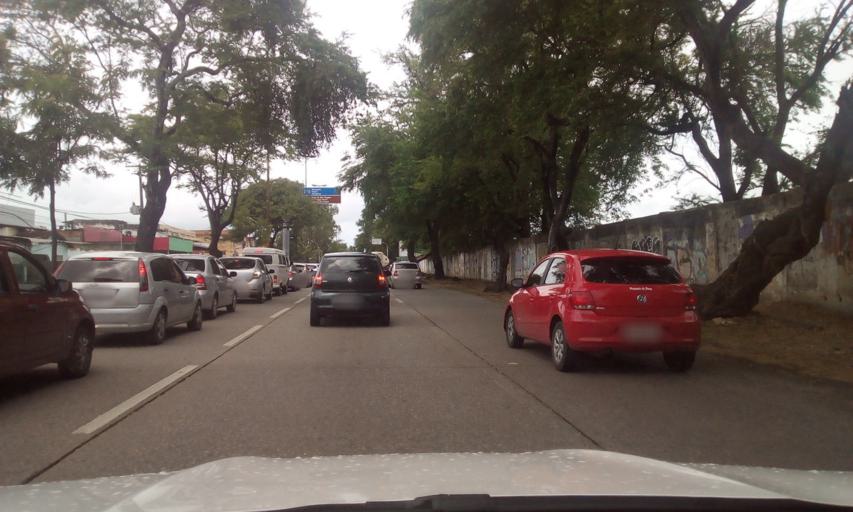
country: BR
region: Pernambuco
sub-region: Recife
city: Recife
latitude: -8.1145
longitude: -34.9256
